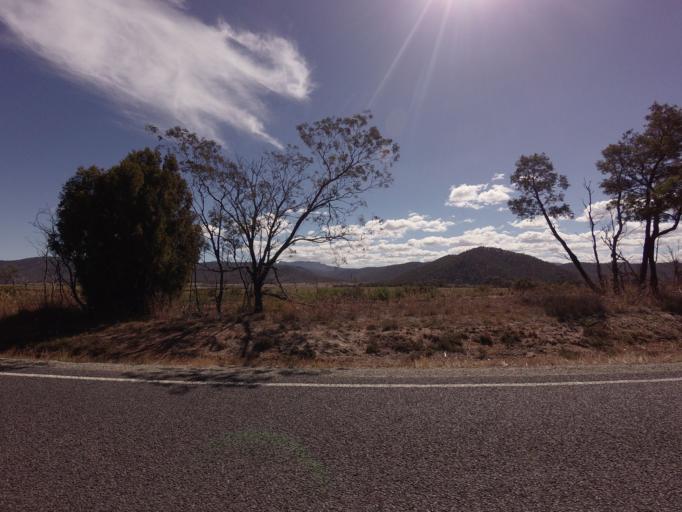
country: AU
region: Tasmania
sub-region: Break O'Day
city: St Helens
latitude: -41.6766
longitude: 147.8944
